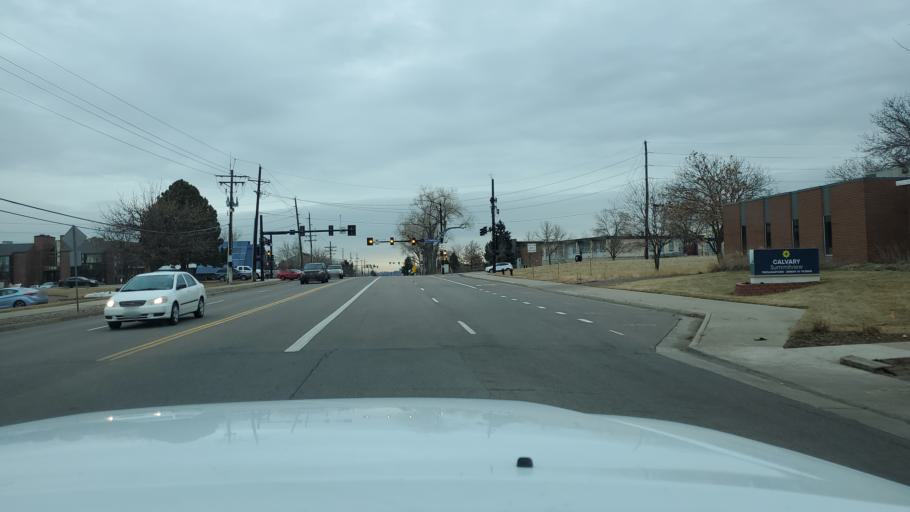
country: US
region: Colorado
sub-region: Arapahoe County
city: Southglenn
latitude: 39.5942
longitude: -104.9414
